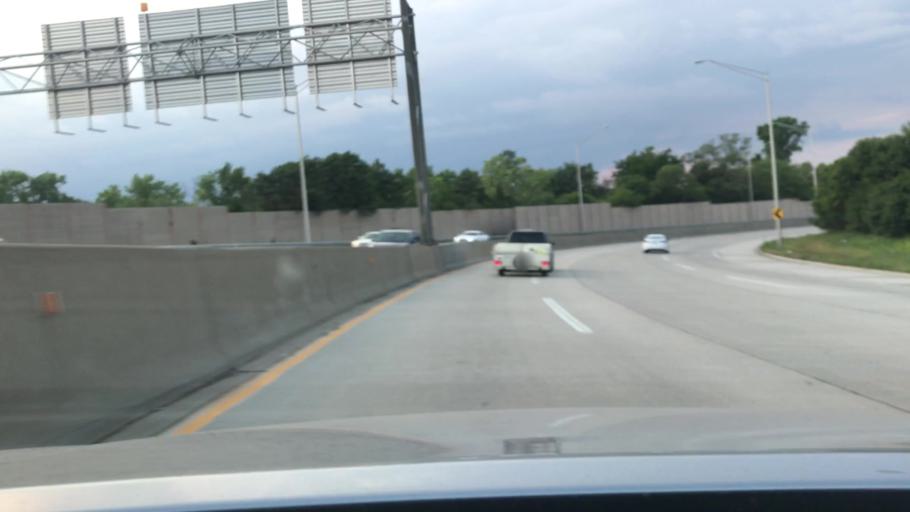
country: US
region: Illinois
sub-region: Cook County
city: Indian Head Park
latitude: 41.7662
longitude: -87.9083
